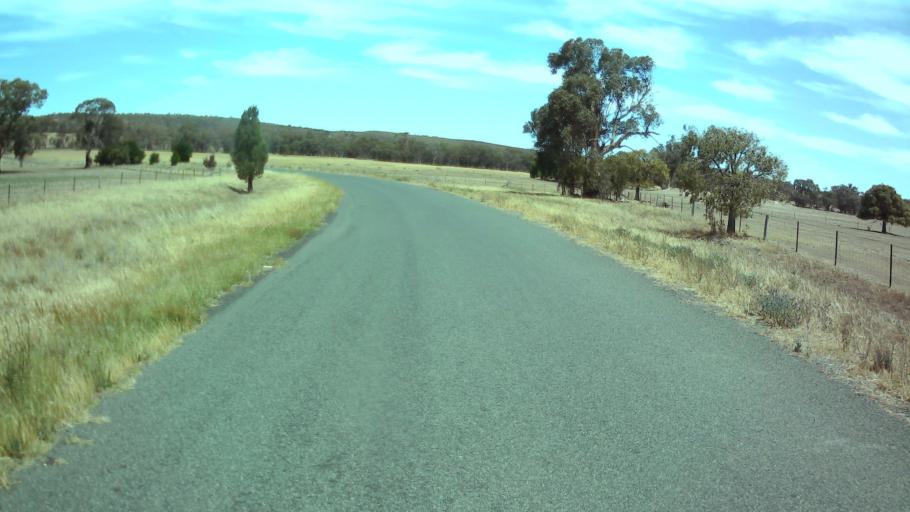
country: AU
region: New South Wales
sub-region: Weddin
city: Grenfell
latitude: -33.8428
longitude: 148.1774
